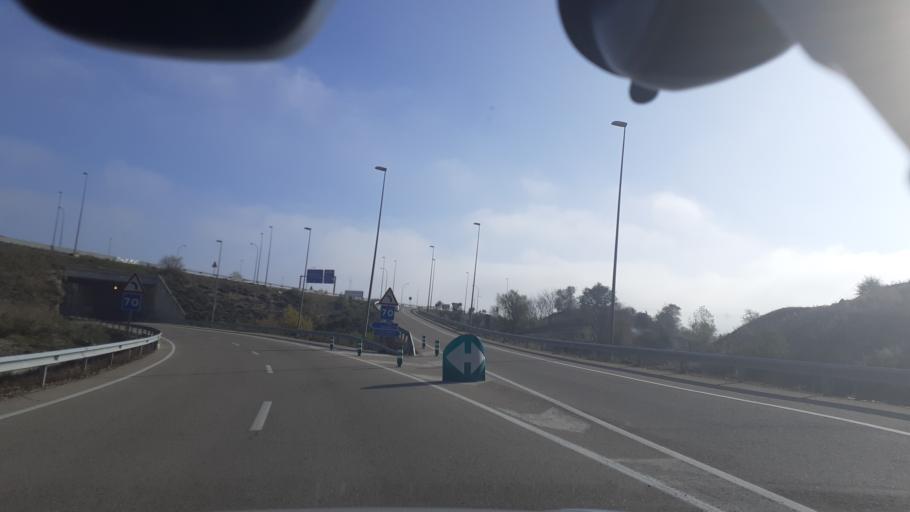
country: ES
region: Madrid
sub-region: Provincia de Madrid
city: Vicalvaro
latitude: 40.4008
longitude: -3.5764
